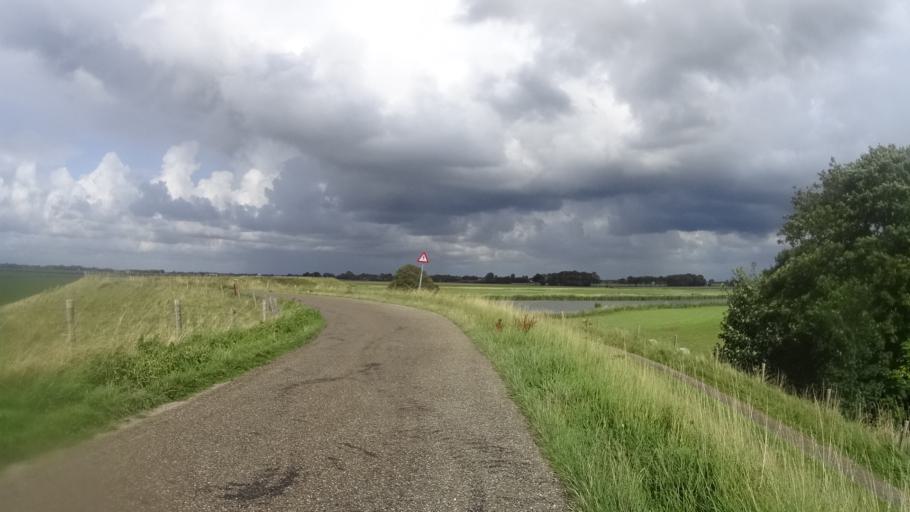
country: NL
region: North Holland
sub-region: Gemeente Schagen
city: Harenkarspel
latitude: 52.7632
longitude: 4.7281
